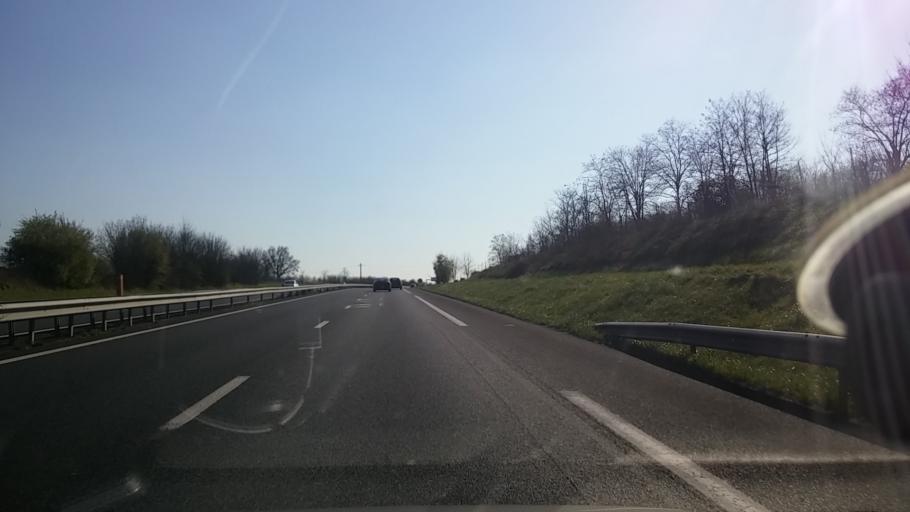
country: FR
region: Centre
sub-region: Departement du Cher
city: Massay
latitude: 47.1440
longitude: 1.9696
